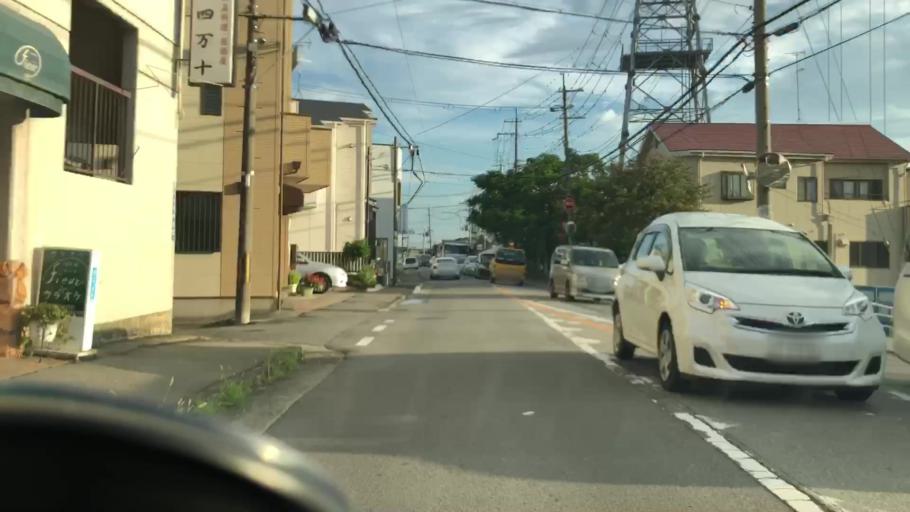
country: JP
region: Hyogo
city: Takarazuka
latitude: 34.7875
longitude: 135.3689
